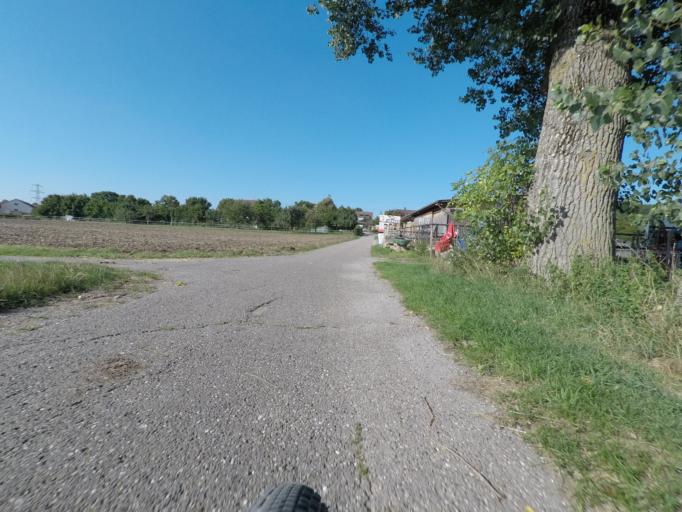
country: DE
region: Baden-Wuerttemberg
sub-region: Regierungsbezirk Stuttgart
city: Ehningen
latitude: 48.6593
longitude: 8.9572
